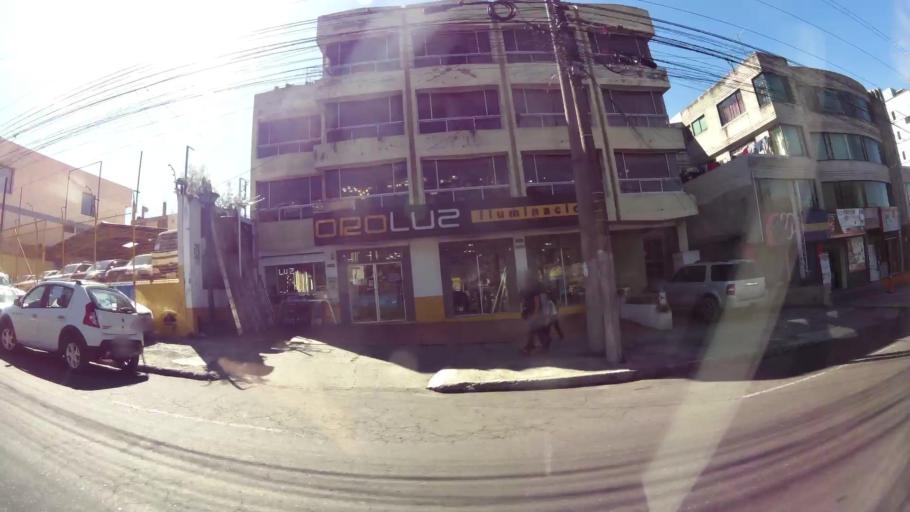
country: EC
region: Pichincha
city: Quito
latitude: -0.1413
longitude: -78.4741
